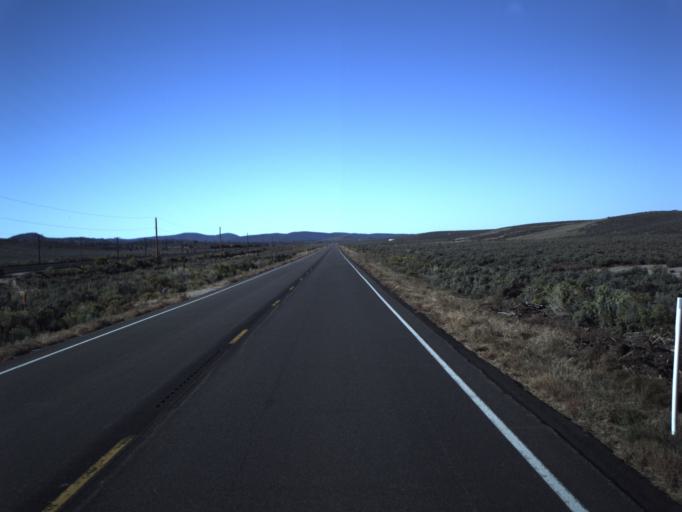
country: US
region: Utah
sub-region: Washington County
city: Enterprise
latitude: 37.7787
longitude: -113.9686
